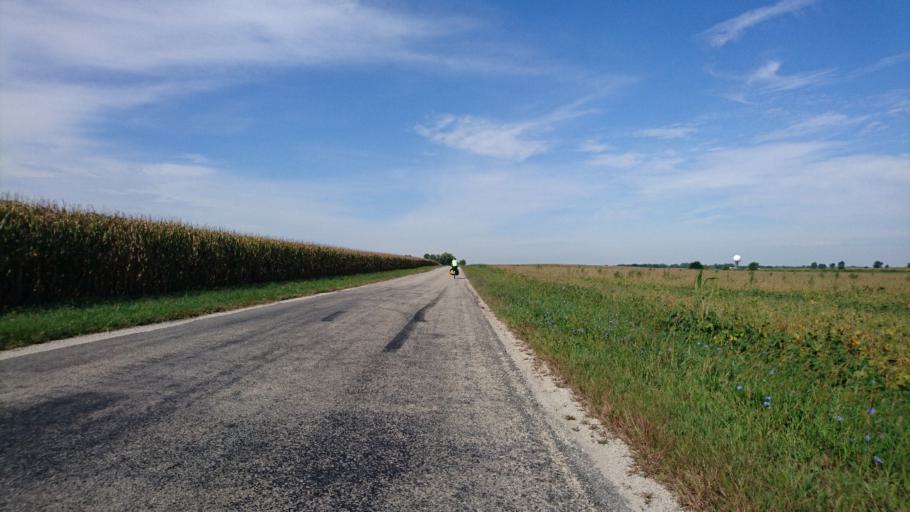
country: US
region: Illinois
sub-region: Will County
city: Manhattan
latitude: 41.4162
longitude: -88.0396
